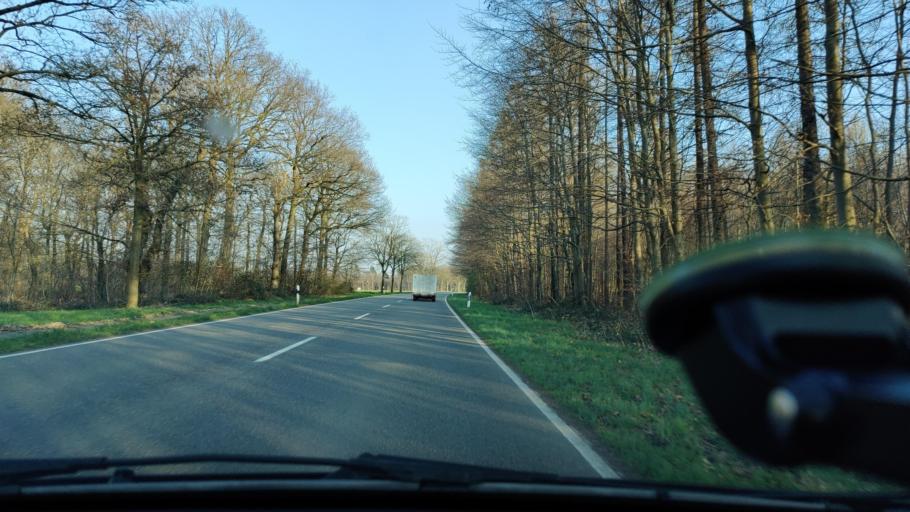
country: DE
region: North Rhine-Westphalia
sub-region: Regierungsbezirk Dusseldorf
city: Issum
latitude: 51.5864
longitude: 6.4267
